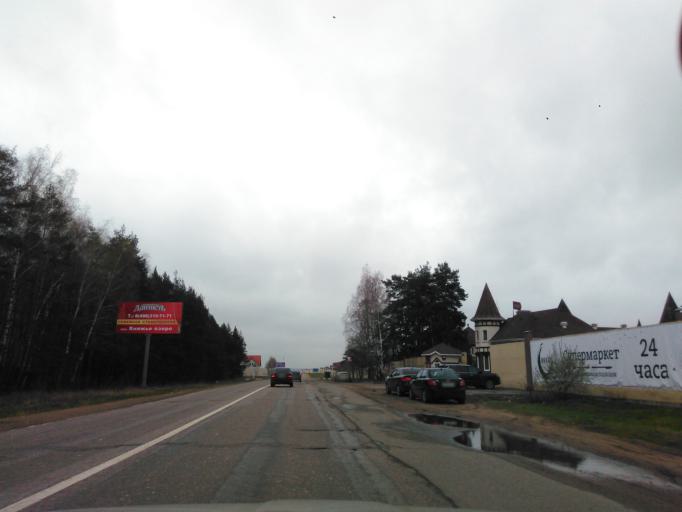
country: RU
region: Moskovskaya
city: Rozhdestveno
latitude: 55.8260
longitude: 37.0409
